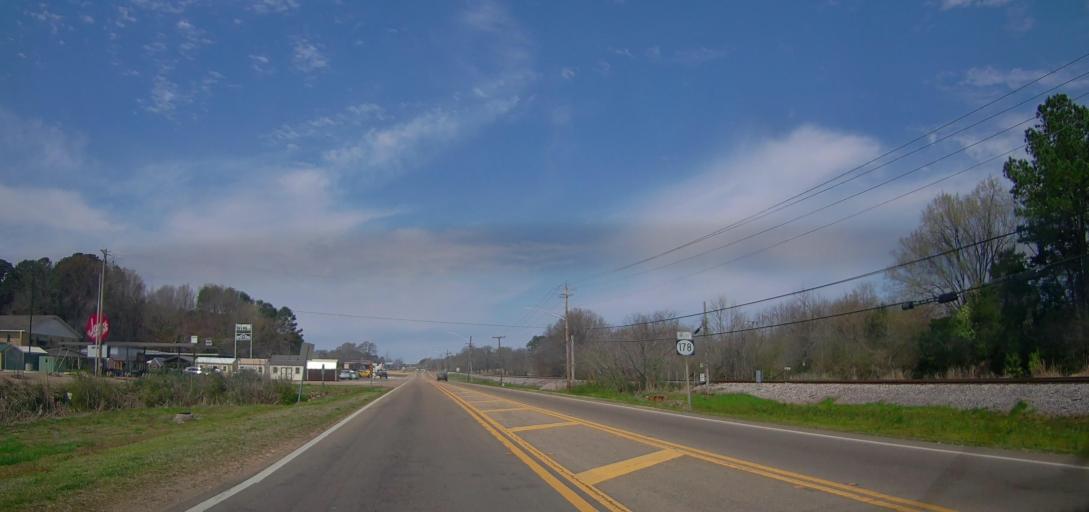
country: US
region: Mississippi
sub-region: Union County
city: New Albany
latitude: 34.5005
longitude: -89.0252
